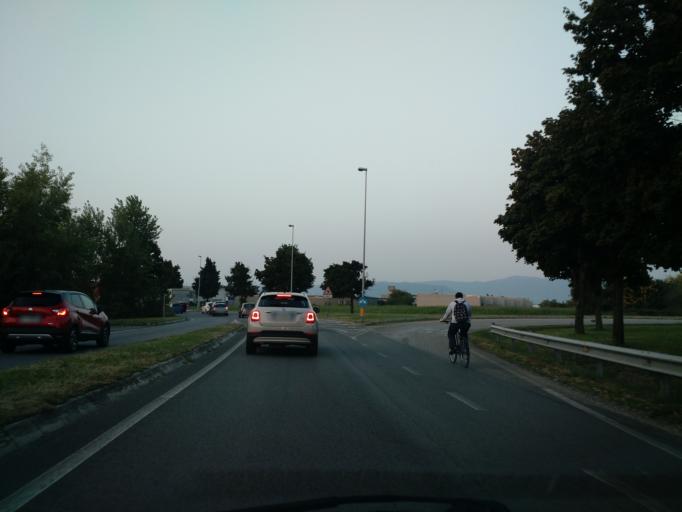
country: IT
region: Veneto
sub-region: Provincia di Vicenza
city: Thiene
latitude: 45.6929
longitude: 11.4816
